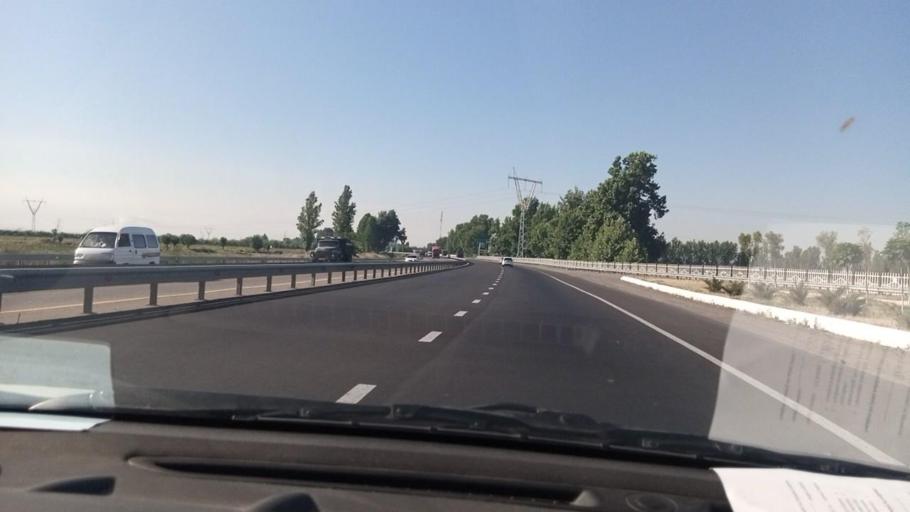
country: UZ
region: Toshkent Shahri
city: Bektemir
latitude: 41.1894
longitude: 69.4032
